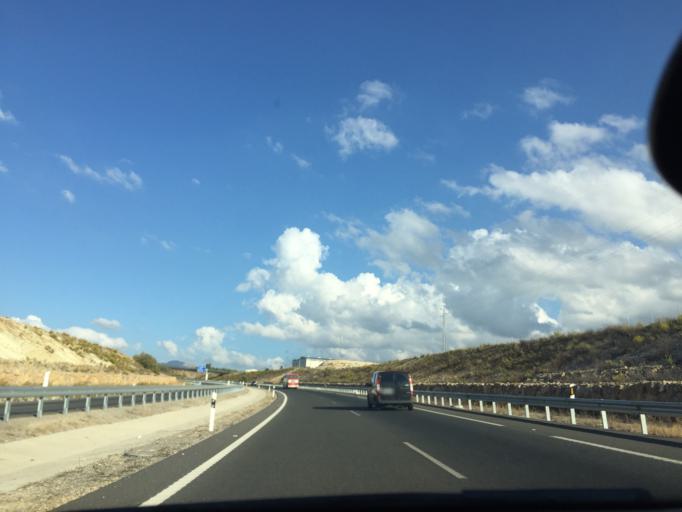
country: ES
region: Andalusia
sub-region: Provincia de Jaen
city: Mancha Real
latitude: 37.8053
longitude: -3.6483
